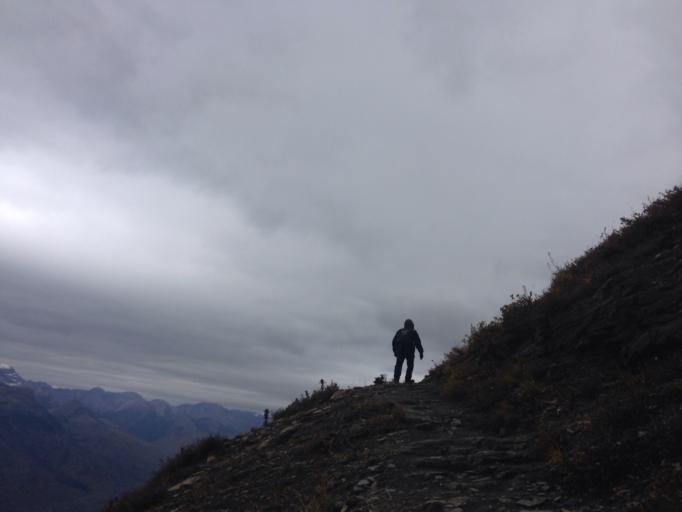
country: US
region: Montana
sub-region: Flathead County
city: Columbia Falls
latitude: 48.7420
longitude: -113.7295
